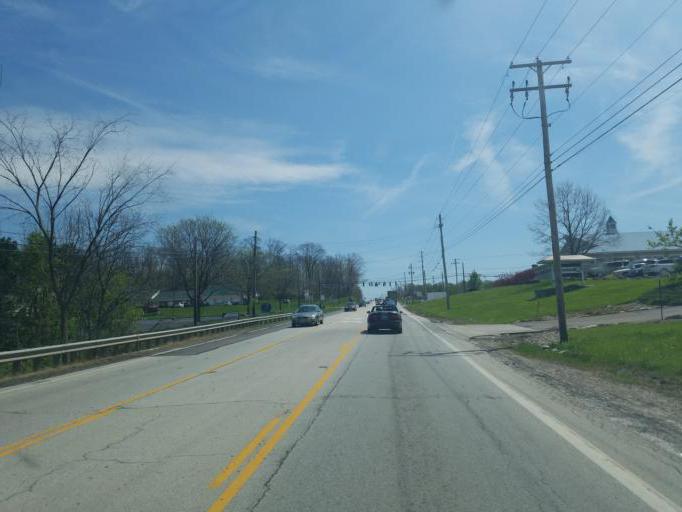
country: US
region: Ohio
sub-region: Medina County
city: Medina
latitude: 41.1364
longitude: -81.8132
